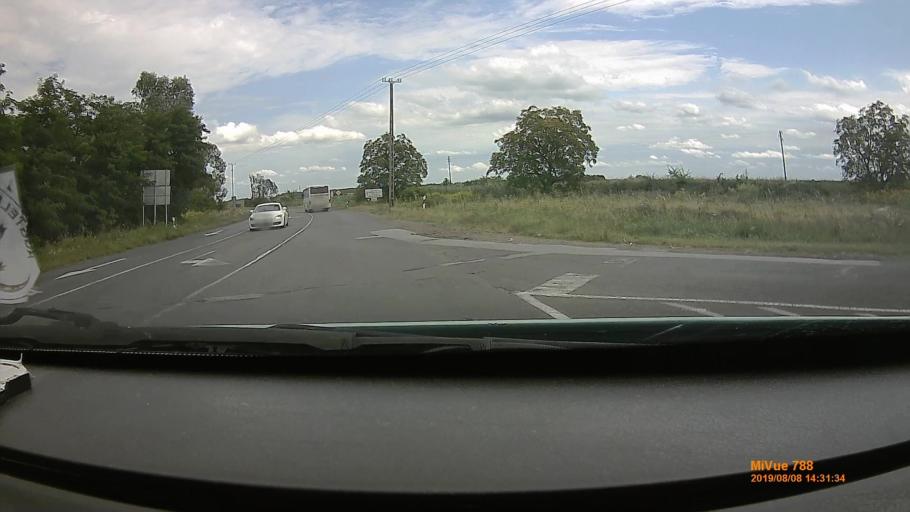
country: HU
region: Szabolcs-Szatmar-Bereg
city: Mateszalka
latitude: 47.9408
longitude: 22.3282
